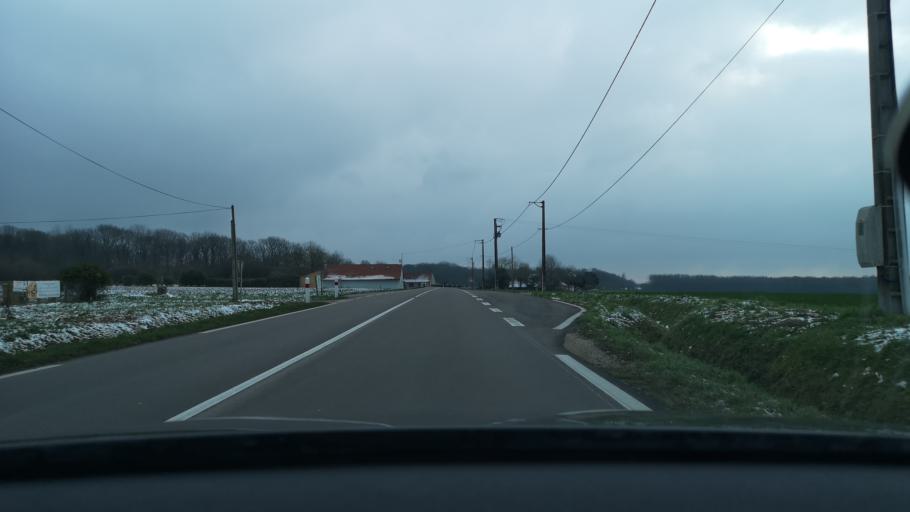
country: FR
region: Bourgogne
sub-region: Departement de Saone-et-Loire
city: Ouroux-sur-Saone
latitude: 46.7707
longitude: 4.9752
